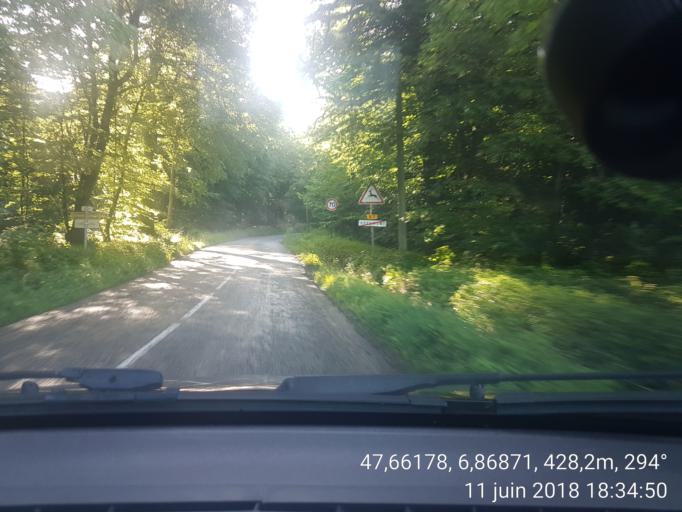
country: FR
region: Franche-Comte
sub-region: Territoire de Belfort
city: Offemont
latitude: 47.6617
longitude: 6.8689
